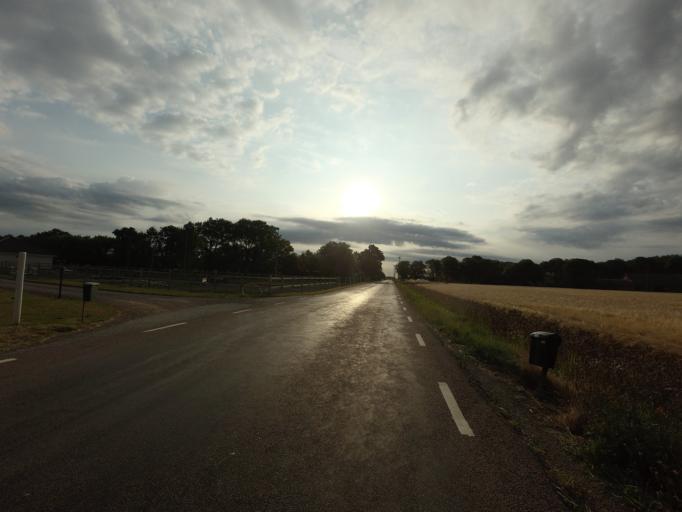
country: SE
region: Skane
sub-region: Helsingborg
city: Odakra
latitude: 56.1543
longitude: 12.6884
